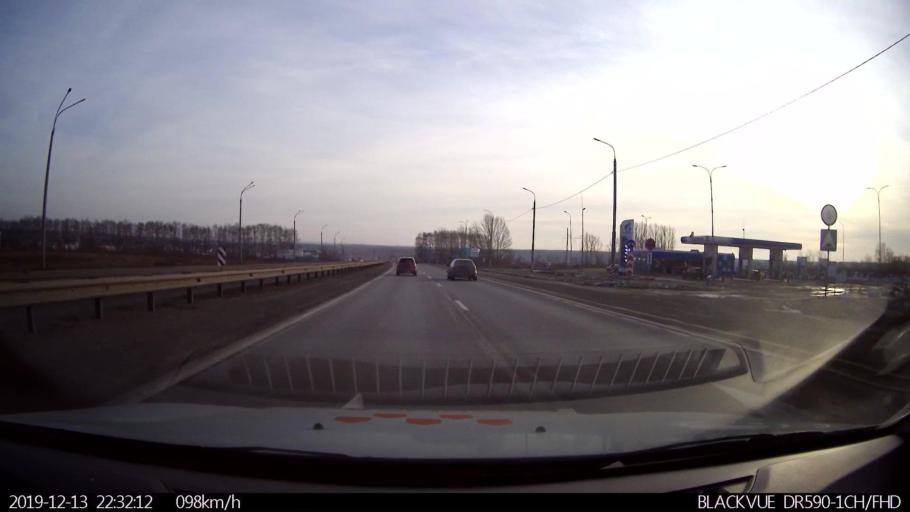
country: RU
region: Nizjnij Novgorod
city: Afonino
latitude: 56.2078
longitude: 44.0866
